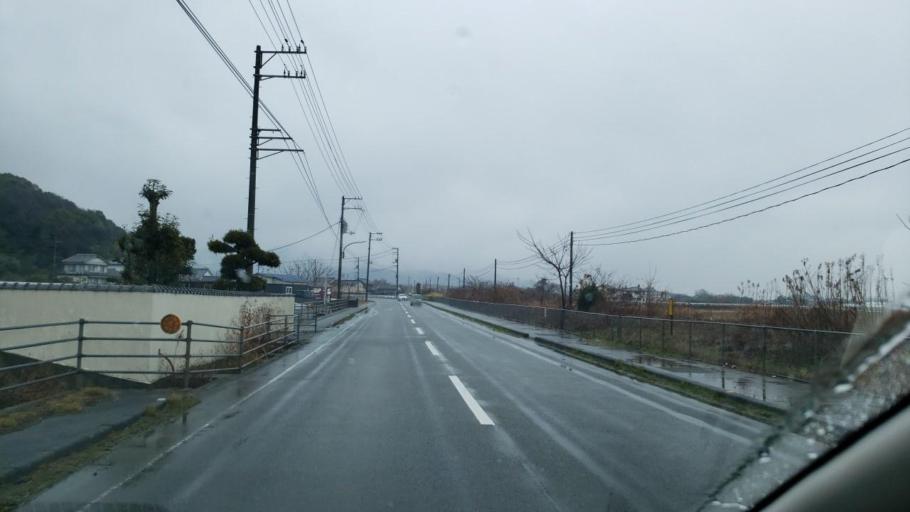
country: JP
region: Tokushima
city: Ishii
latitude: 34.1511
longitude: 134.4881
